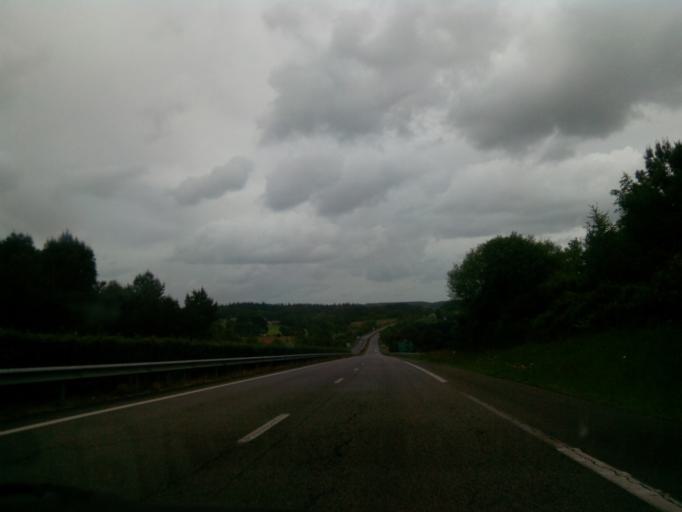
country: FR
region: Brittany
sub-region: Departement du Morbihan
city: Molac
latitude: 47.7847
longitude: -2.4561
